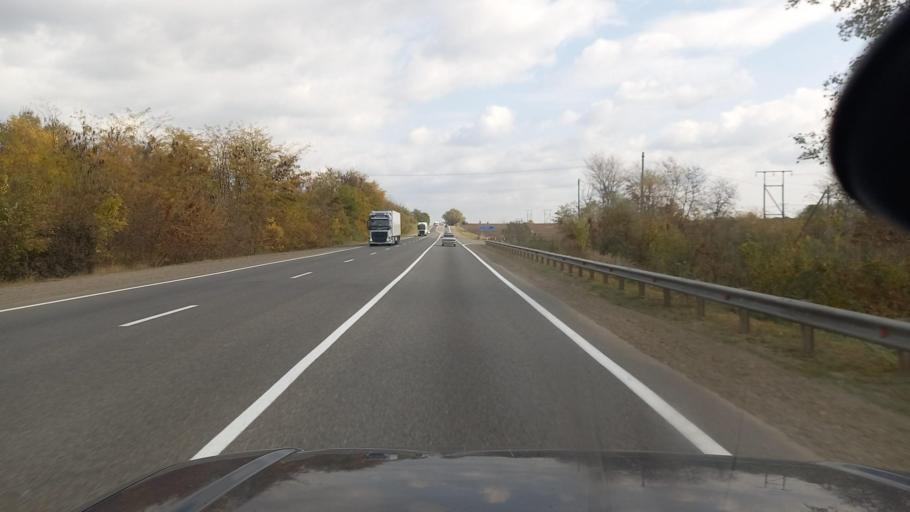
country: RU
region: Krasnodarskiy
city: Chernomorskiy
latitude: 44.8542
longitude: 38.4535
